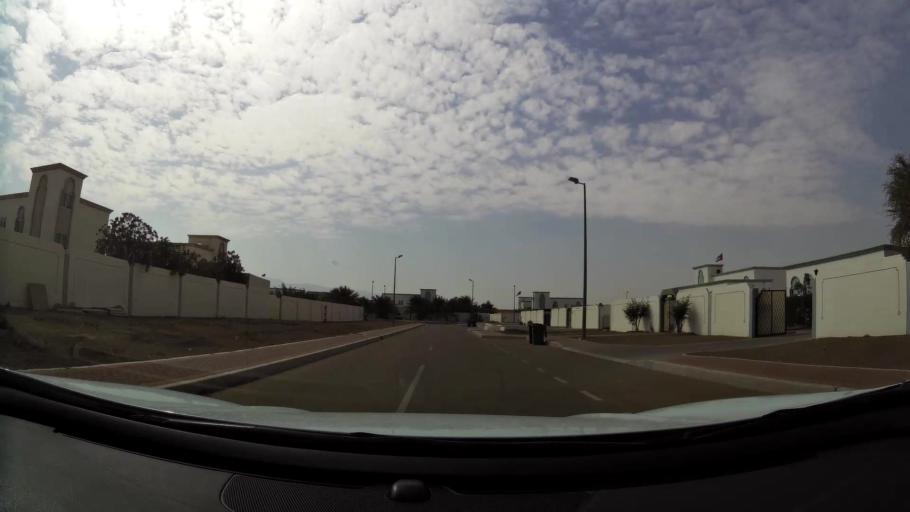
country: AE
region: Abu Dhabi
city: Al Ain
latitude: 24.1007
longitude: 55.8904
